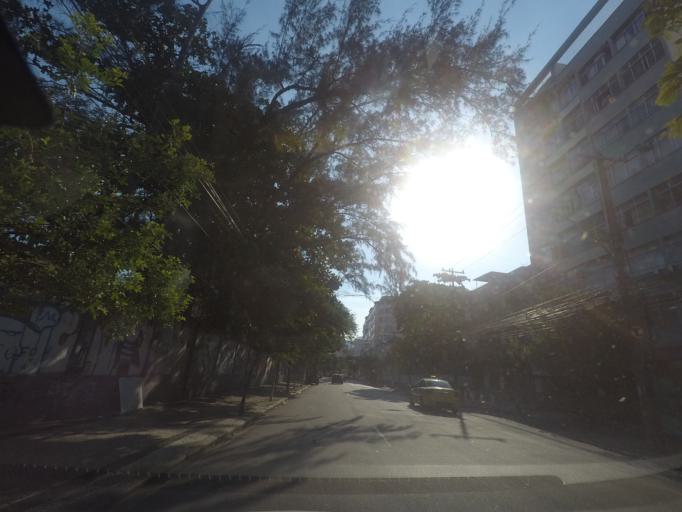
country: BR
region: Rio de Janeiro
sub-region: Rio De Janeiro
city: Rio de Janeiro
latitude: -22.9136
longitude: -43.2178
